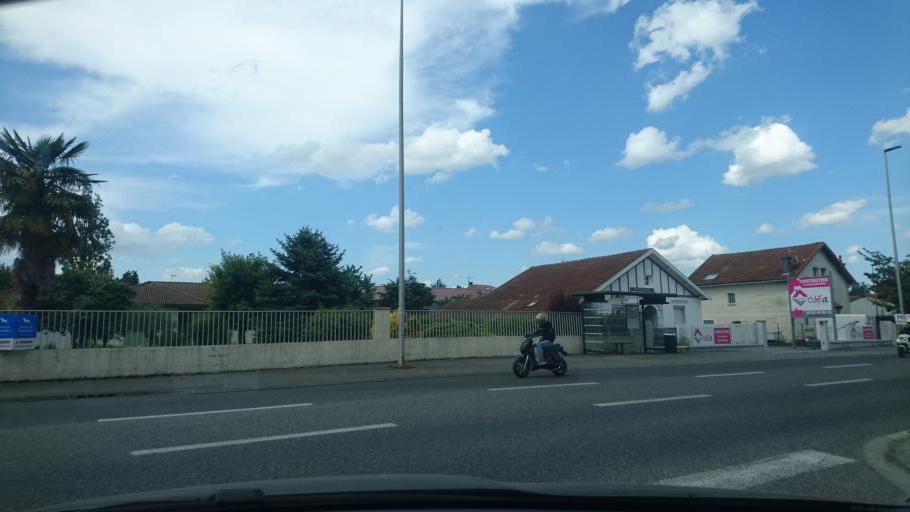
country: FR
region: Midi-Pyrenees
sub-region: Departement des Hautes-Pyrenees
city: Ibos
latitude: 43.2391
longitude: 0.0302
